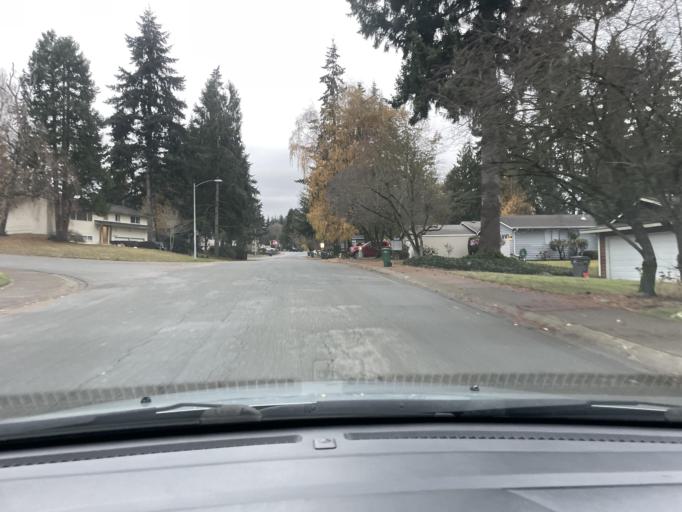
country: US
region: Washington
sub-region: King County
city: Kingsgate
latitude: 47.7217
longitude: -122.1789
